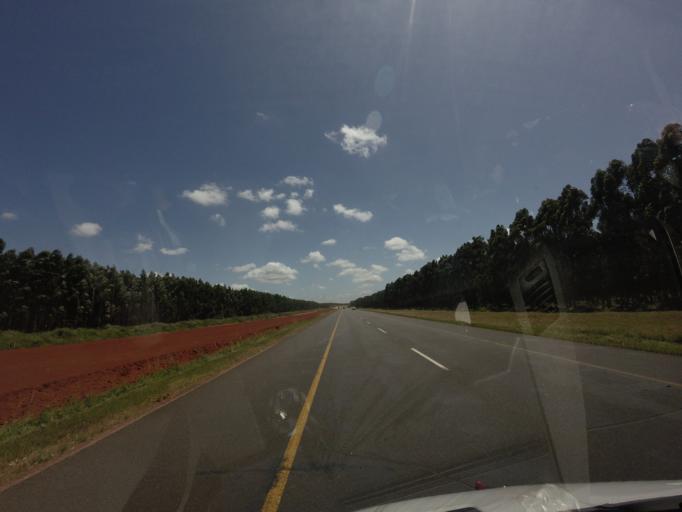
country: ZA
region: KwaZulu-Natal
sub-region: uThungulu District Municipality
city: Empangeni
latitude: -28.7503
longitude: 31.9362
